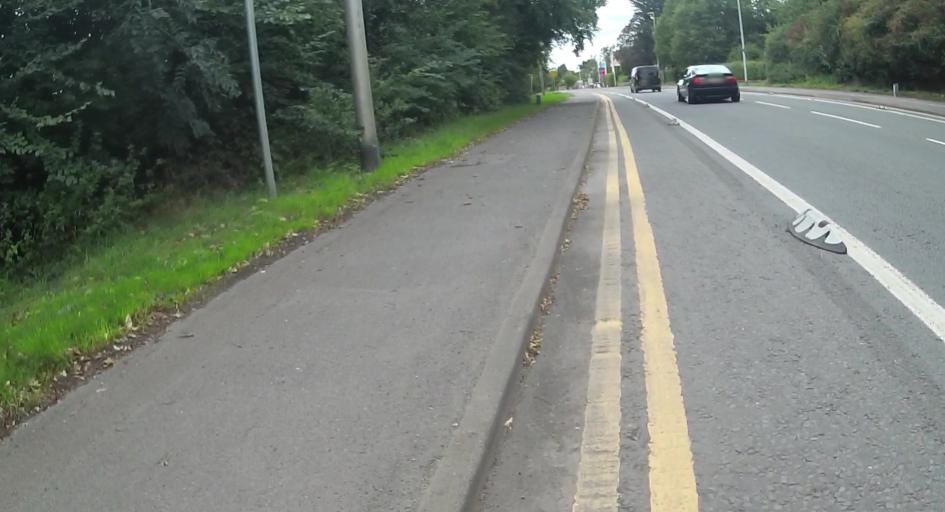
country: GB
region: England
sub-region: West Berkshire
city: Thatcham
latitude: 51.4035
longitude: -1.2443
